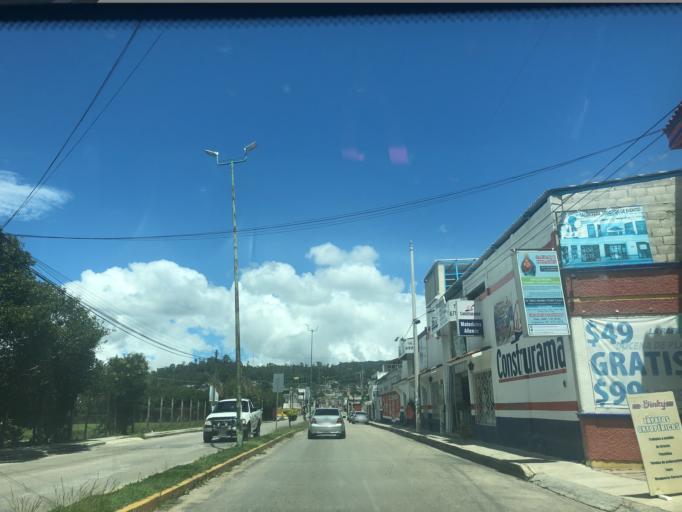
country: MX
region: Chiapas
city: San Cristobal de las Casas
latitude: 16.7228
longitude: -92.6402
